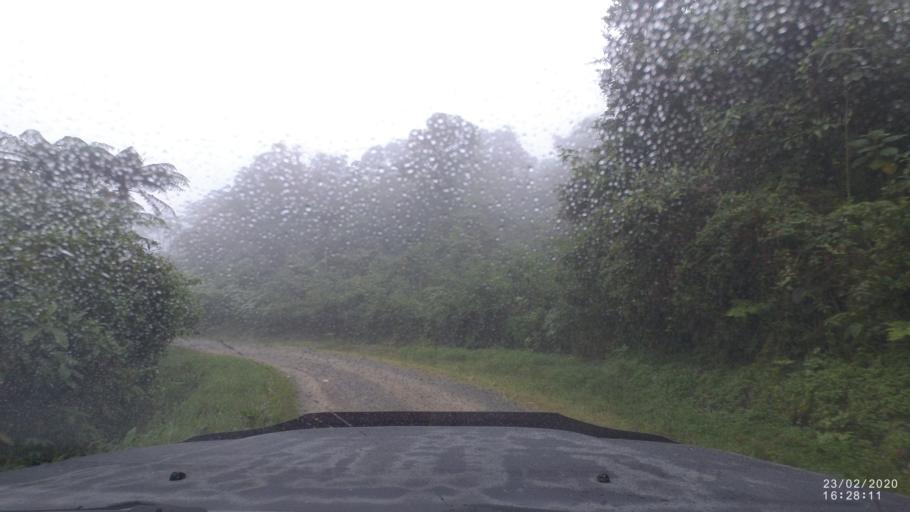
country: BO
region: Cochabamba
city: Colomi
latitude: -17.0989
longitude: -65.9830
